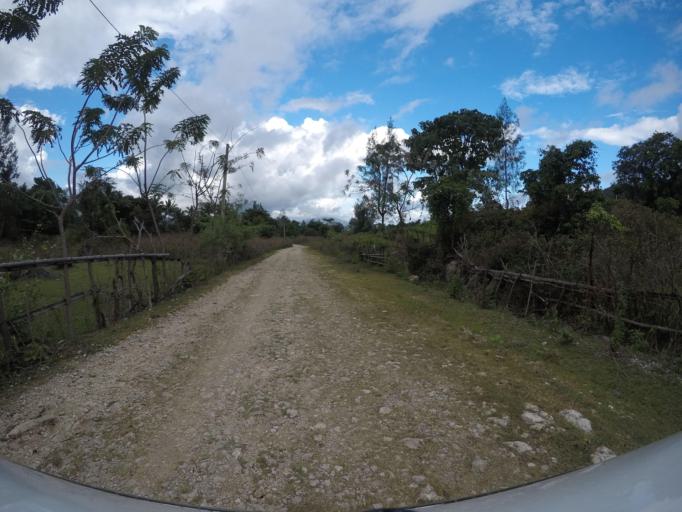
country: TL
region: Baucau
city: Venilale
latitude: -8.6809
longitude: 126.6375
